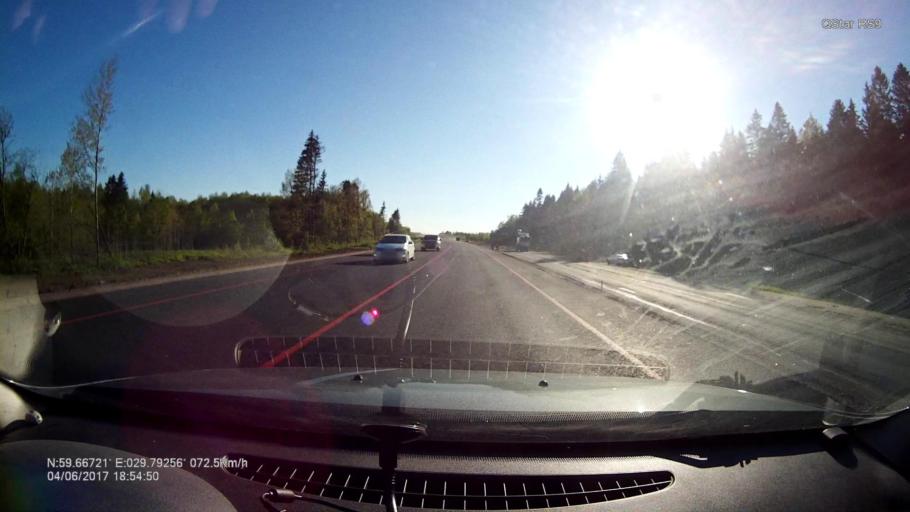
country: RU
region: Leningrad
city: Kipen'
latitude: 59.6672
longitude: 29.7924
